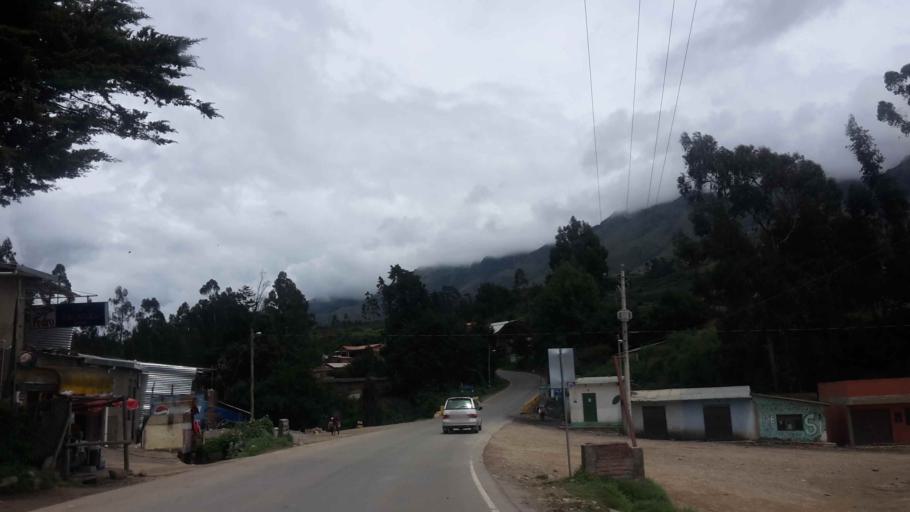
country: BO
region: Cochabamba
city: Totora
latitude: -17.5320
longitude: -65.3779
